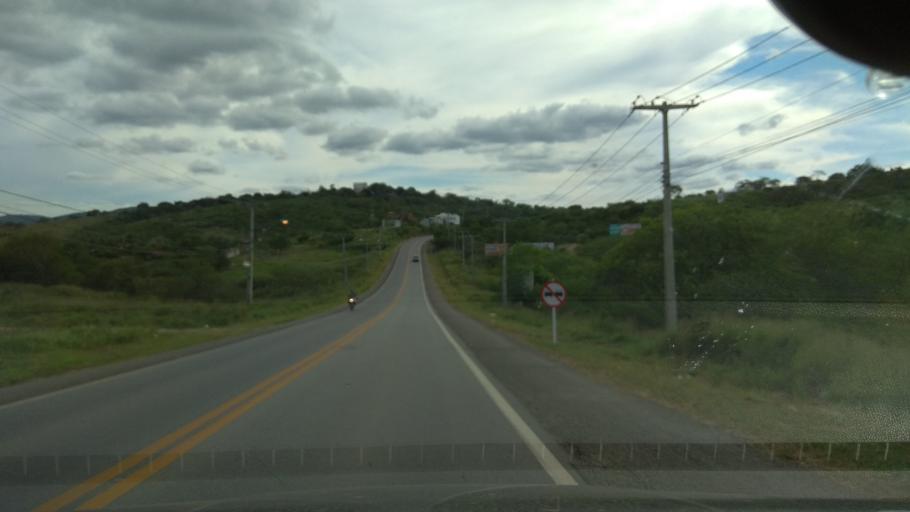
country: BR
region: Bahia
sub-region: Jequie
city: Jequie
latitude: -13.8713
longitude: -40.0461
